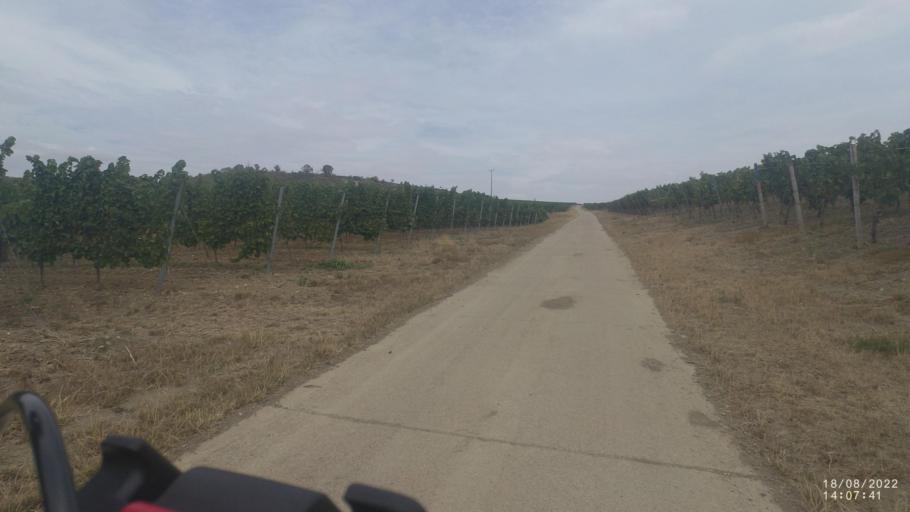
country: DE
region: Rheinland-Pfalz
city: Vendersheim
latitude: 49.8591
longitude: 8.0757
